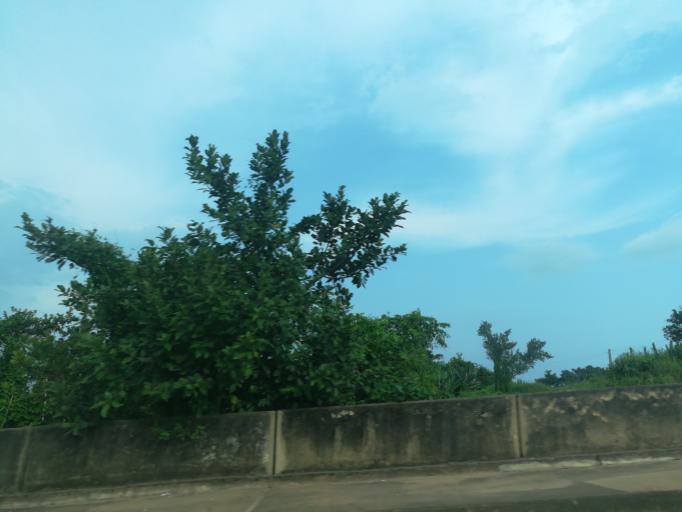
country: NG
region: Lagos
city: Ikorodu
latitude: 6.6247
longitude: 3.6634
